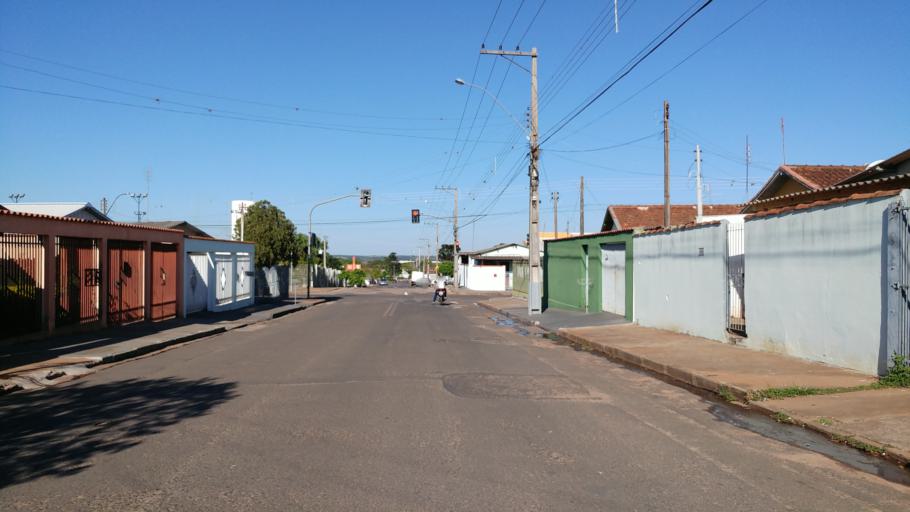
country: BR
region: Sao Paulo
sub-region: Paraguacu Paulista
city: Paraguacu Paulista
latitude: -22.4240
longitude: -50.5765
